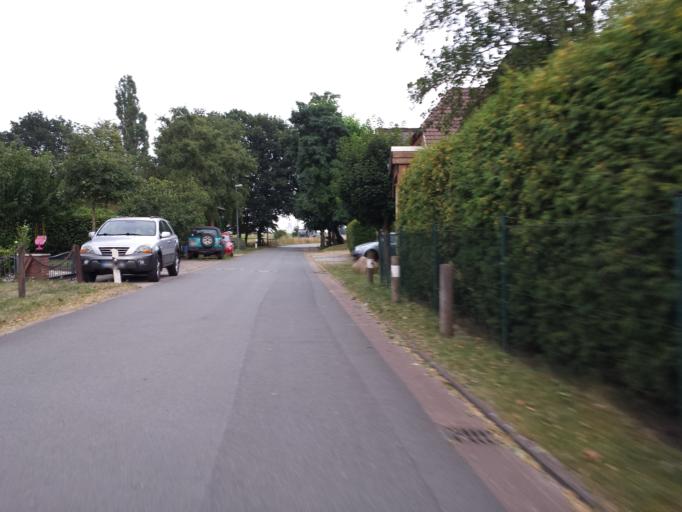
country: DE
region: Lower Saxony
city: Ritterhude
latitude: 53.1179
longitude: 8.6929
